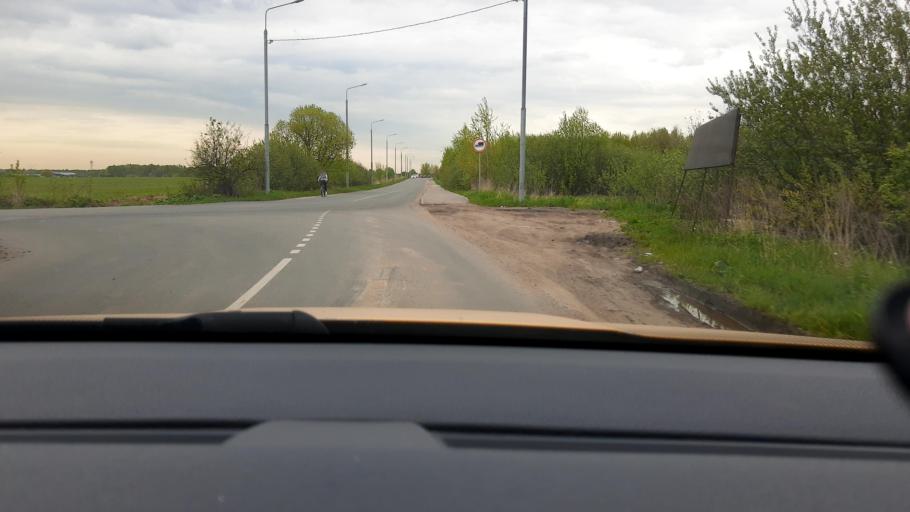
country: RU
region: Moskovskaya
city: Novopodrezkovo
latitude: 55.9350
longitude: 37.3805
